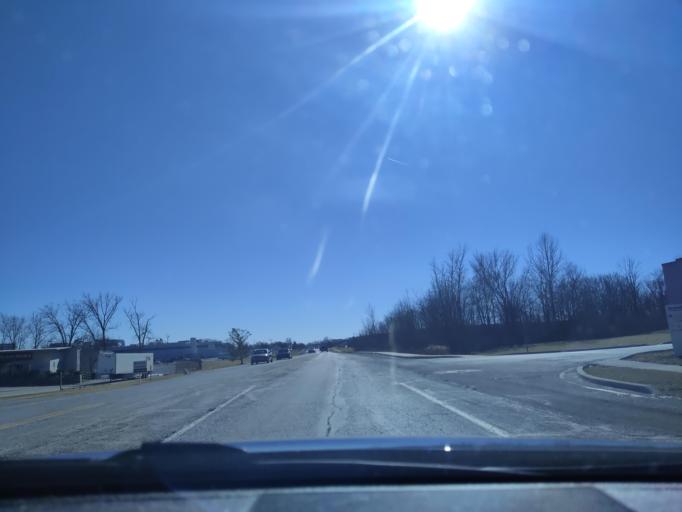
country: US
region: Indiana
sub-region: Boone County
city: Zionsville
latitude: 39.8927
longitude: -86.2418
